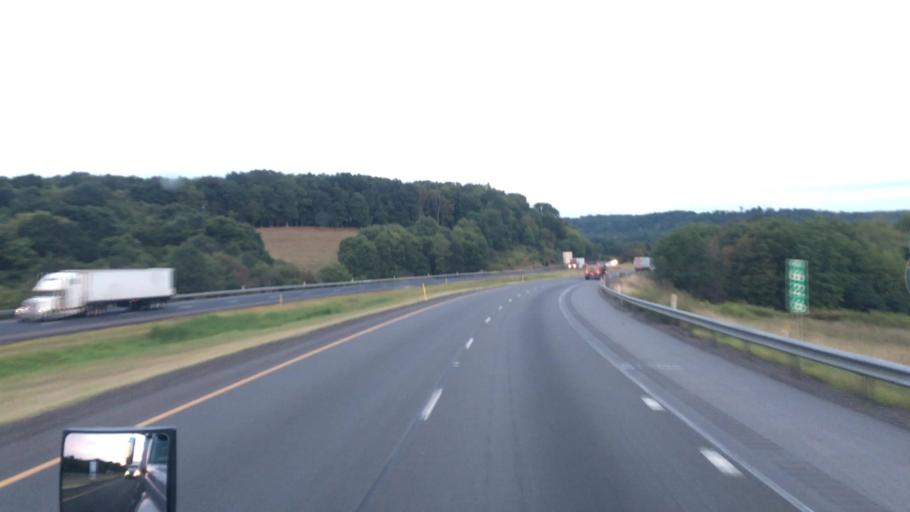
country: US
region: Pennsylvania
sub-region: Clarion County
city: Clarion
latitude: 41.1840
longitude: -79.3847
